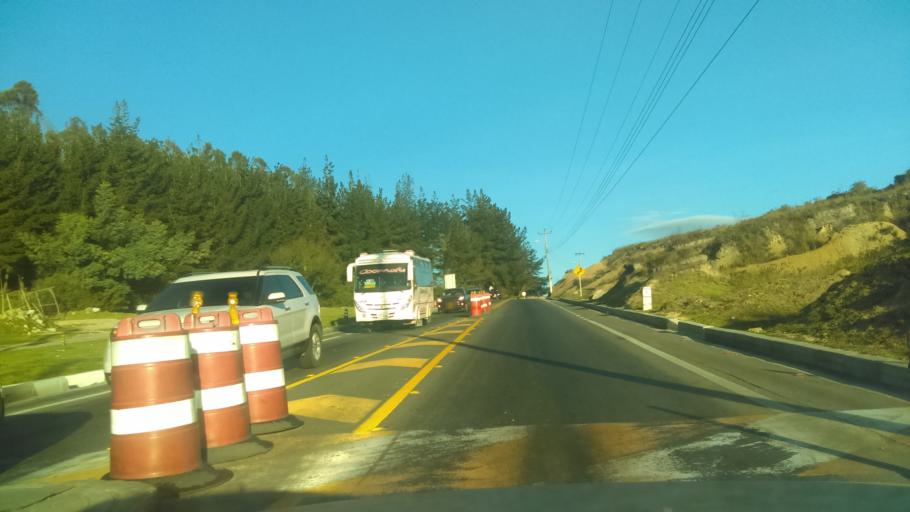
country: CO
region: Cundinamarca
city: San Antonio del Tequendama
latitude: 4.6275
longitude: -74.2902
